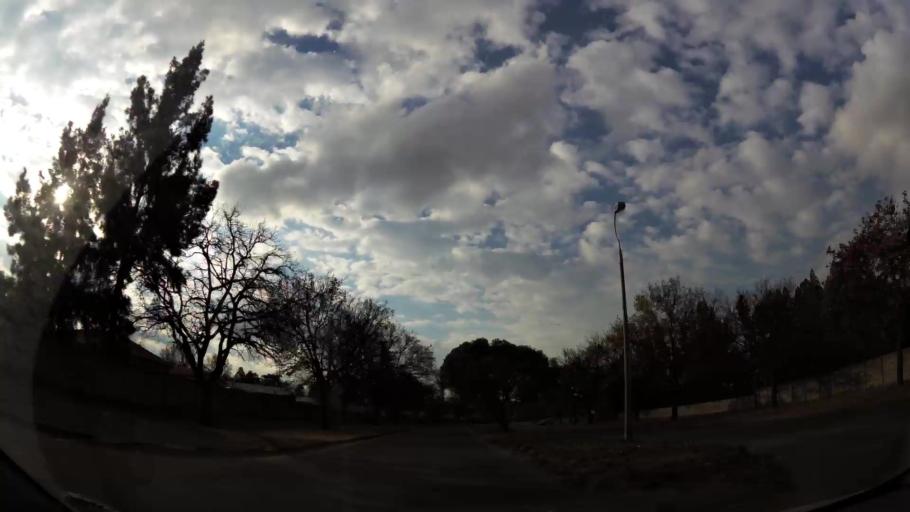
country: ZA
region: Orange Free State
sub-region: Fezile Dabi District Municipality
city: Sasolburg
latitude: -26.8146
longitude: 27.8194
